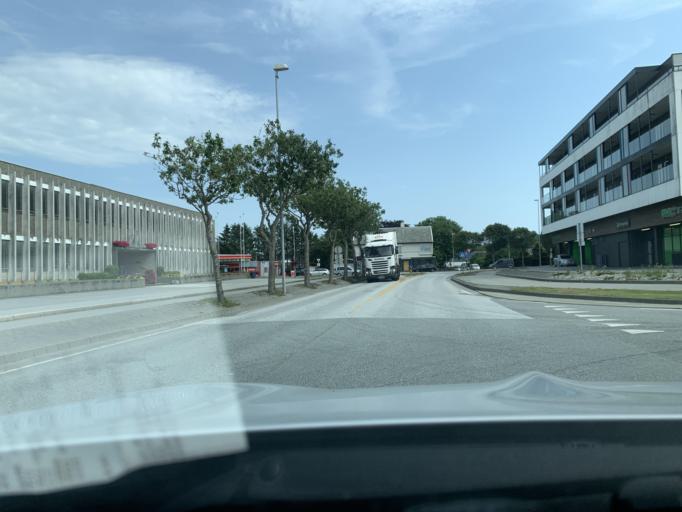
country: NO
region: Rogaland
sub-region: Klepp
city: Kleppe
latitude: 58.7766
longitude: 5.6290
